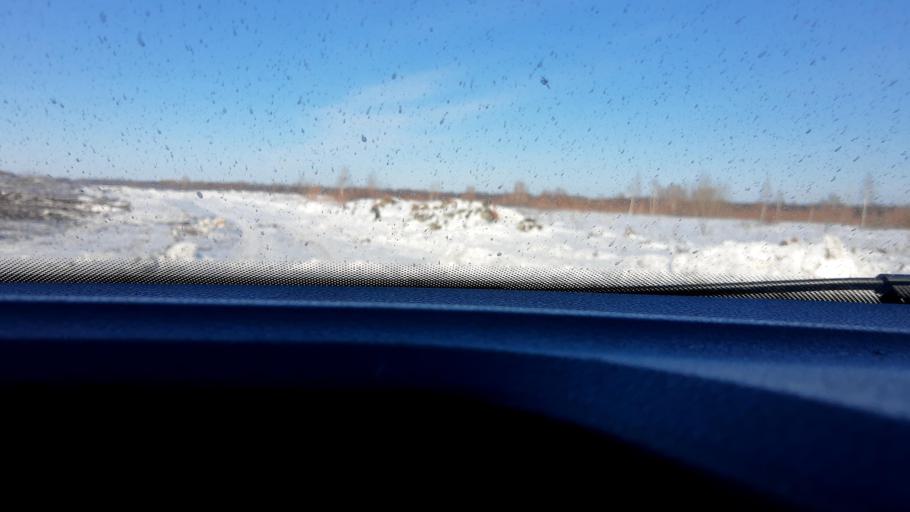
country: RU
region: Bashkortostan
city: Mikhaylovka
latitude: 54.7195
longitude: 55.8364
